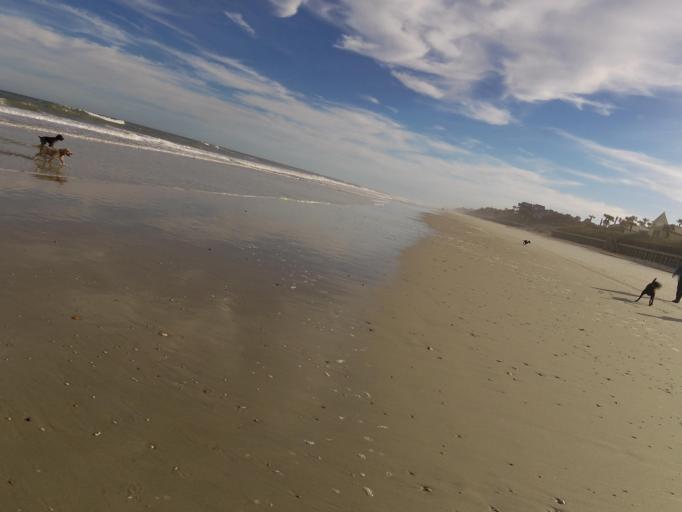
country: US
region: Florida
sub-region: Saint Johns County
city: Sawgrass
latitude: 30.1811
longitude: -81.3596
